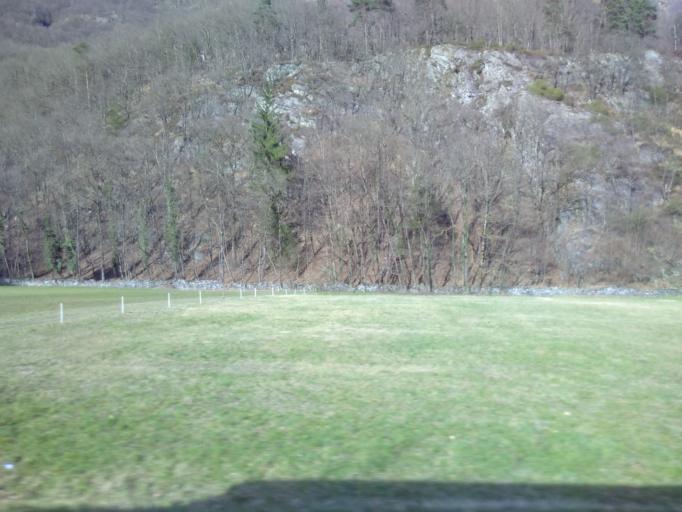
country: CH
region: Ticino
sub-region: Locarno District
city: Verscio
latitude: 46.2356
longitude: 8.7225
